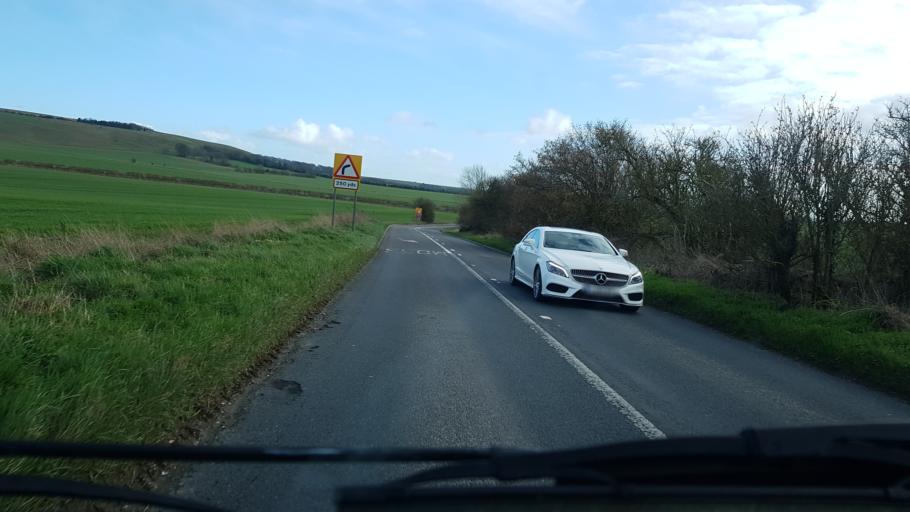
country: GB
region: England
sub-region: Wiltshire
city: Avebury
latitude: 51.4628
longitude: -1.8476
